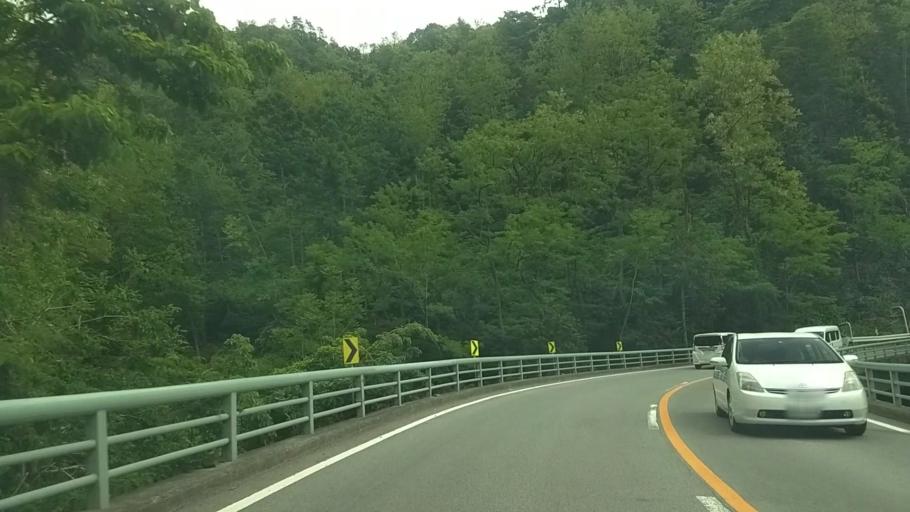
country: JP
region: Yamanashi
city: Isawa
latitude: 35.5644
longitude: 138.5945
